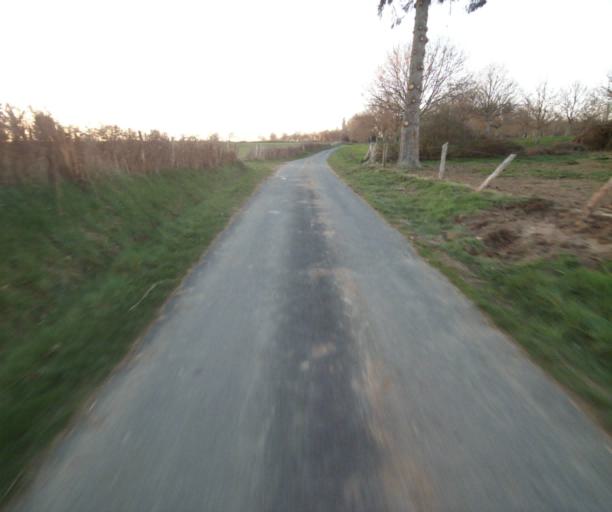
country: FR
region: Limousin
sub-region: Departement de la Correze
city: Uzerche
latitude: 45.3682
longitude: 1.6152
